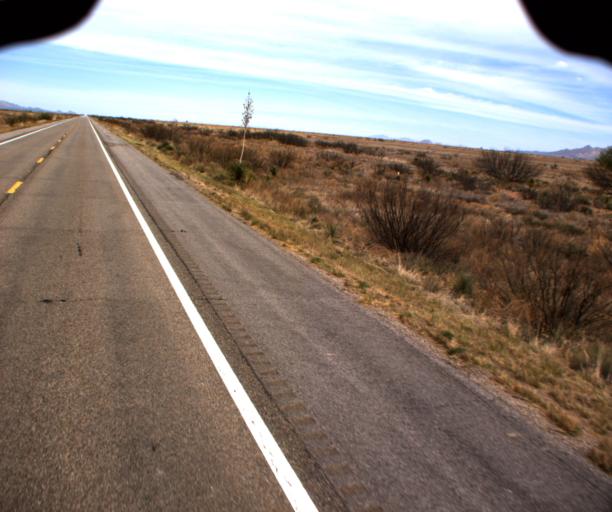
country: US
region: Arizona
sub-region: Cochise County
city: Pirtleville
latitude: 31.5126
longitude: -109.6417
